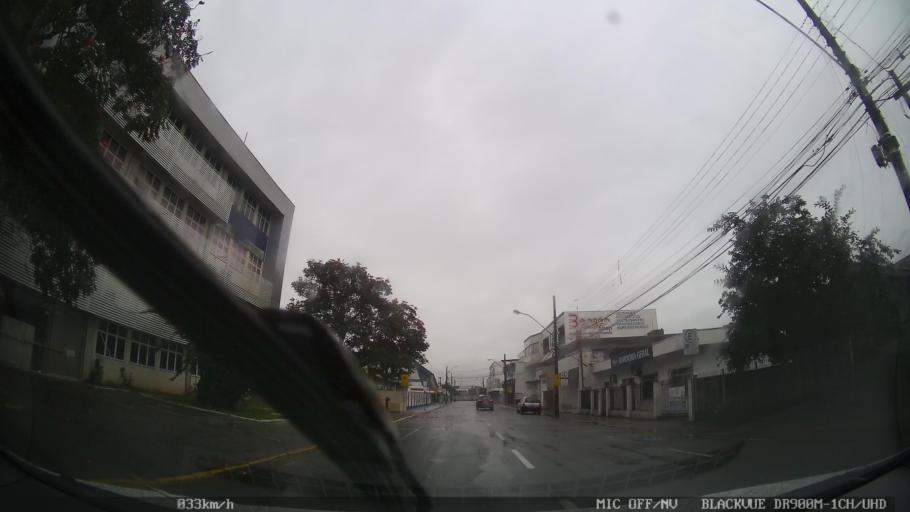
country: BR
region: Santa Catarina
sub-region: Itajai
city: Itajai
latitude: -26.9038
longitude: -48.6687
